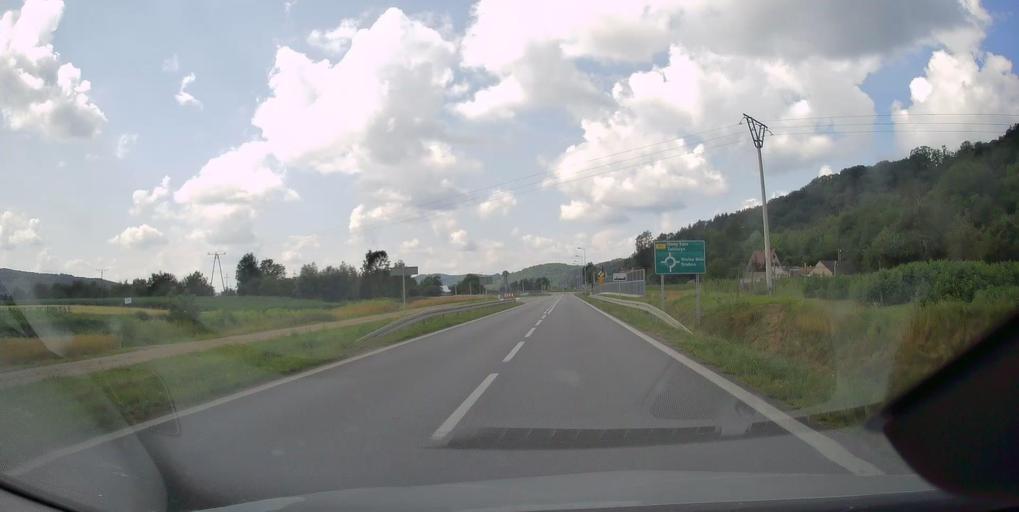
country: PL
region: Lesser Poland Voivodeship
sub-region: Powiat tarnowski
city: Wielka Wies
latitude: 49.9265
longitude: 20.8357
